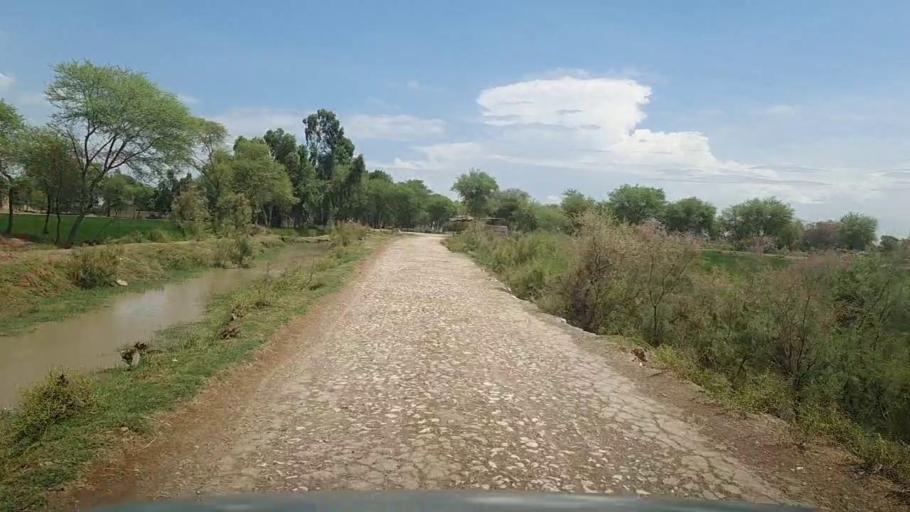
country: PK
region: Sindh
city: Kandhkot
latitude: 28.3408
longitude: 69.2418
